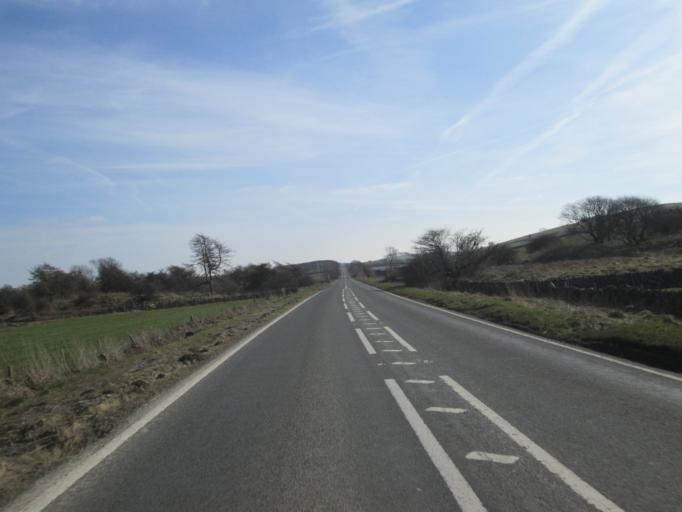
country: GB
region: England
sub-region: Derbyshire
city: Bakewell
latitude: 53.1646
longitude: -1.7760
